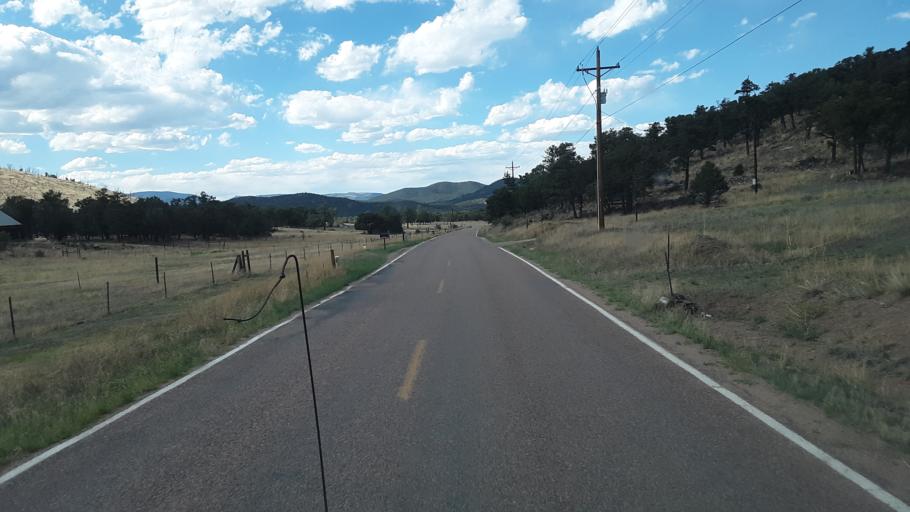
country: US
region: Colorado
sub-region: Custer County
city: Westcliffe
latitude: 38.3304
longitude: -105.4851
